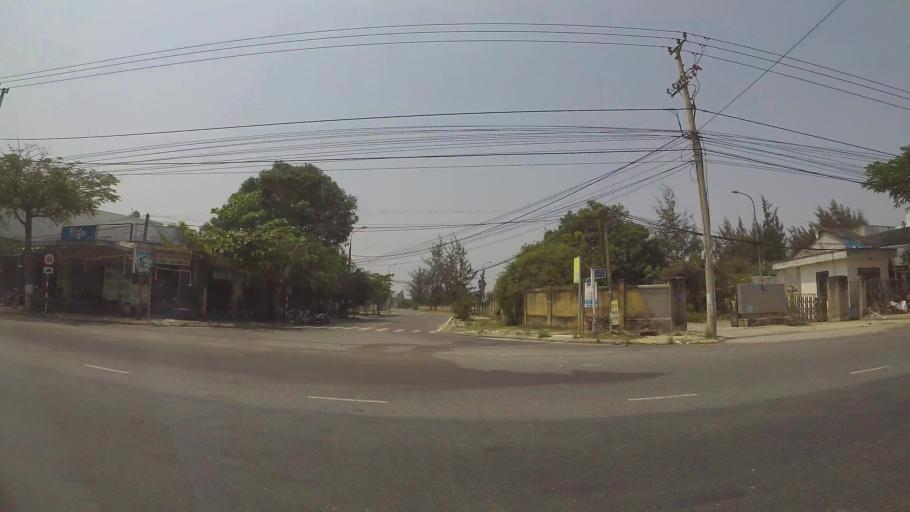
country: VN
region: Da Nang
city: Ngu Hanh Son
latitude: 15.9816
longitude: 108.2557
